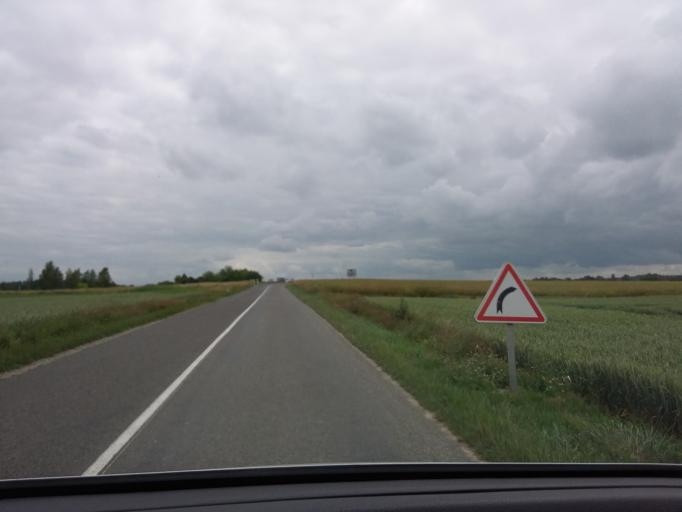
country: FR
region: Champagne-Ardenne
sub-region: Departement de la Marne
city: Cormicy
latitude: 49.4117
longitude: 3.8812
